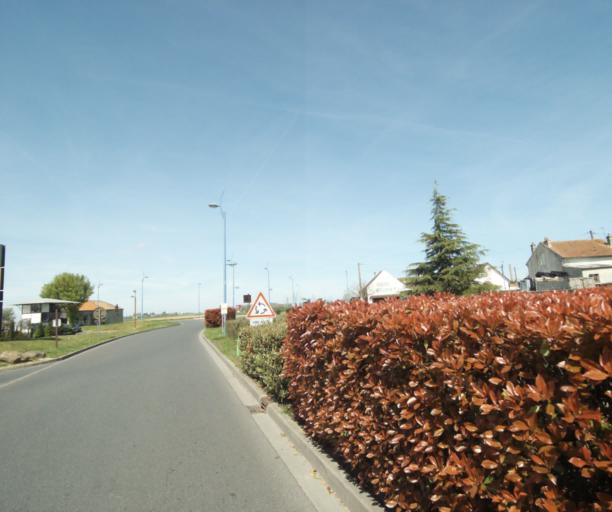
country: FR
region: Ile-de-France
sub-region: Departement de Seine-et-Marne
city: Nangis
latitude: 48.5558
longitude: 3.0052
